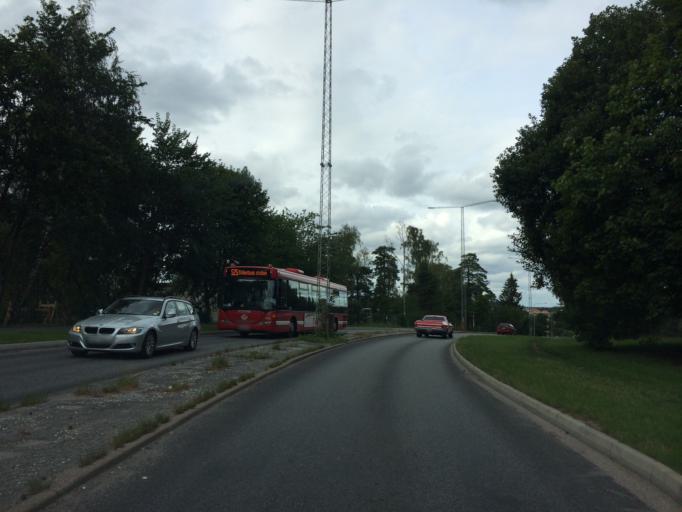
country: SE
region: Stockholm
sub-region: Sollentuna Kommun
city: Sollentuna
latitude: 59.4323
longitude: 17.9494
